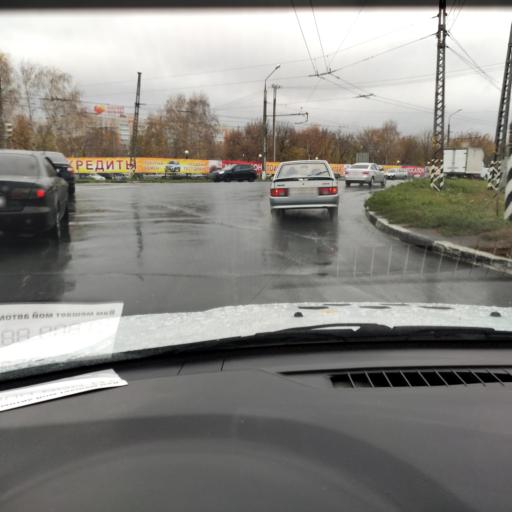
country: RU
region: Samara
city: Tol'yatti
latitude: 53.5510
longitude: 49.3174
